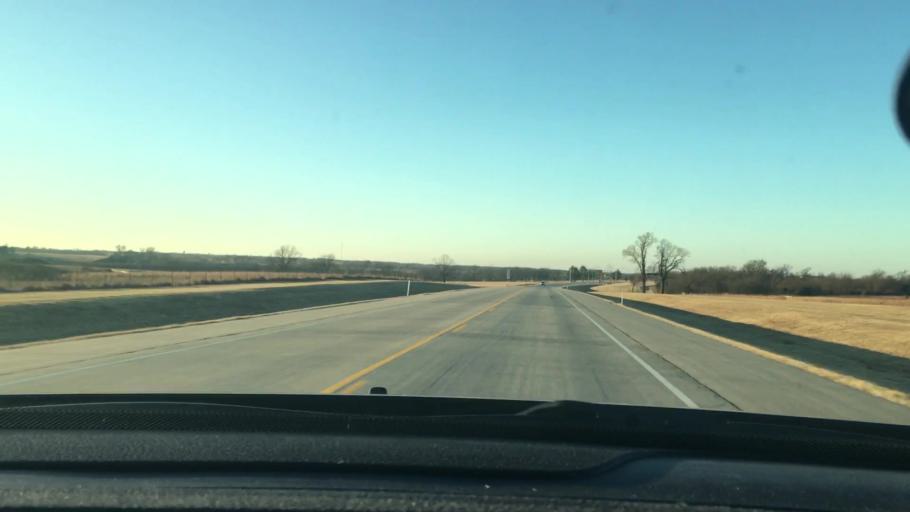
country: US
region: Oklahoma
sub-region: Murray County
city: Sulphur
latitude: 34.5744
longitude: -96.9255
